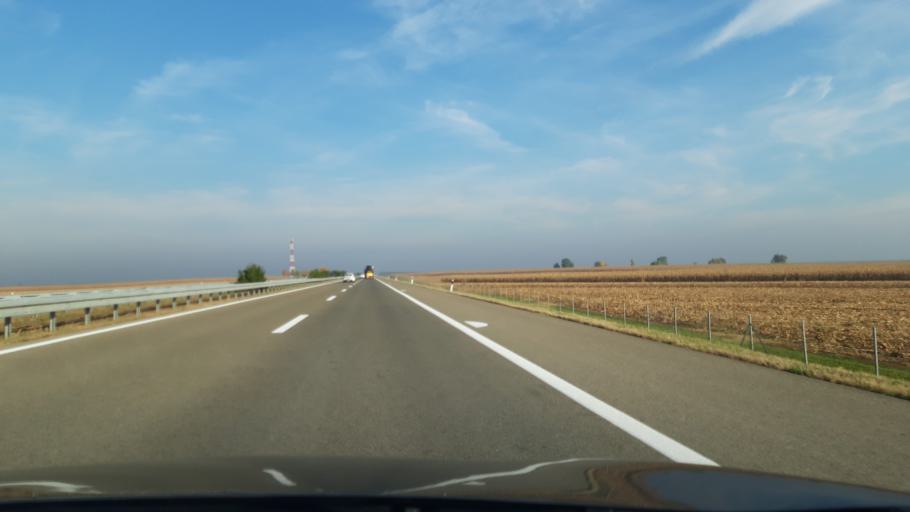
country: RS
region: Autonomna Pokrajina Vojvodina
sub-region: Severnobacki Okrug
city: Backa Topola
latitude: 45.8811
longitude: 19.6999
